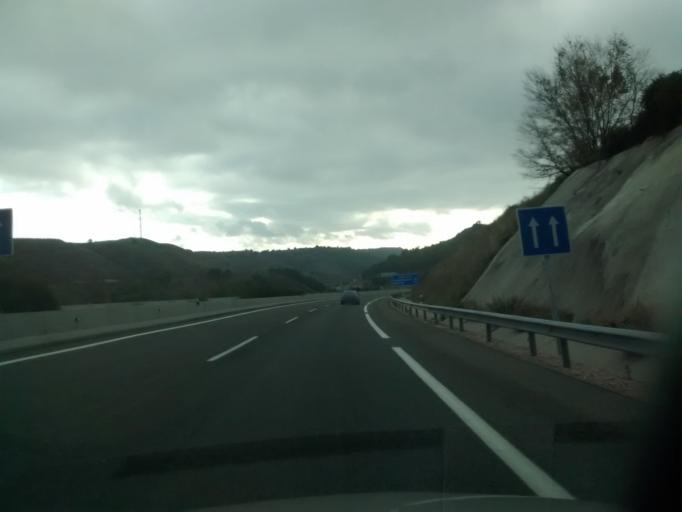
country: ES
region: Castille-La Mancha
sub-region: Provincia de Guadalajara
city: Torija
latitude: 40.7419
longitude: -3.0358
